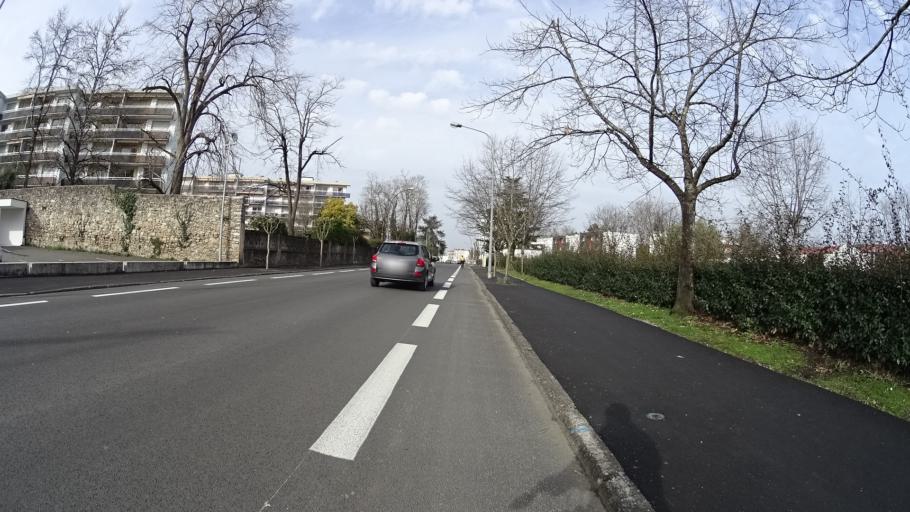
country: FR
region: Aquitaine
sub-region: Departement des Landes
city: Dax
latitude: 43.7002
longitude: -1.0546
